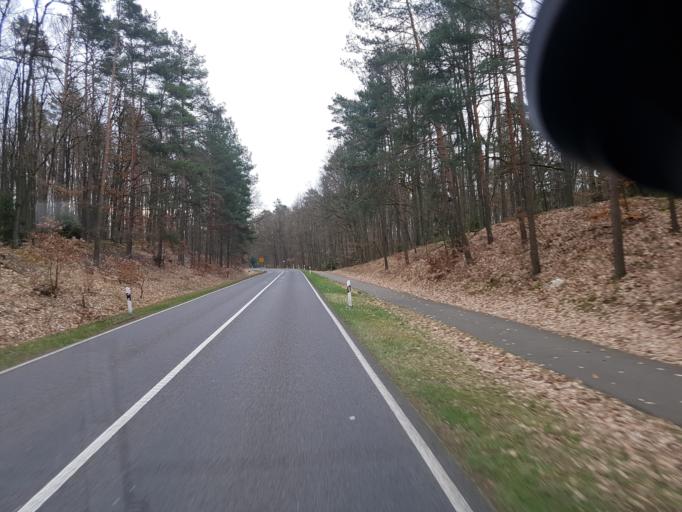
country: DE
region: Brandenburg
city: Gross Lindow
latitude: 52.1734
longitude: 14.4854
